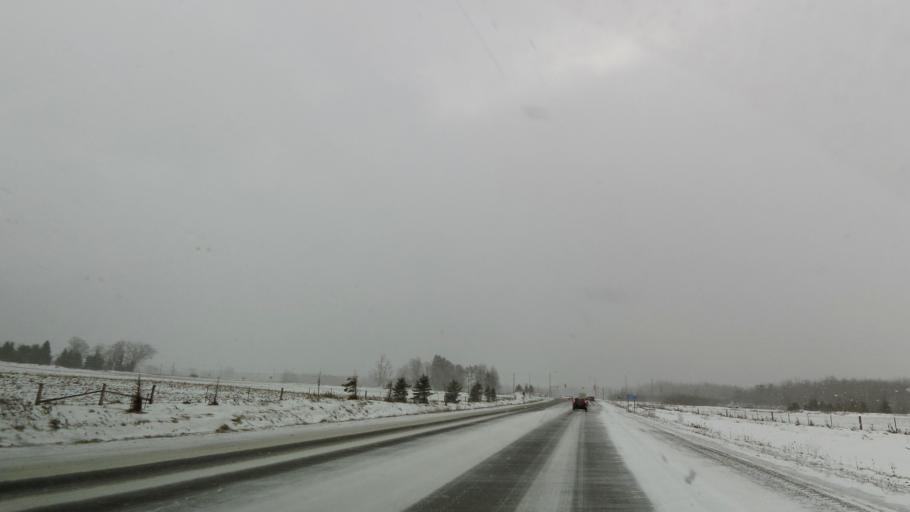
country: CA
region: Ontario
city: Orangeville
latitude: 43.9006
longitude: -80.0952
